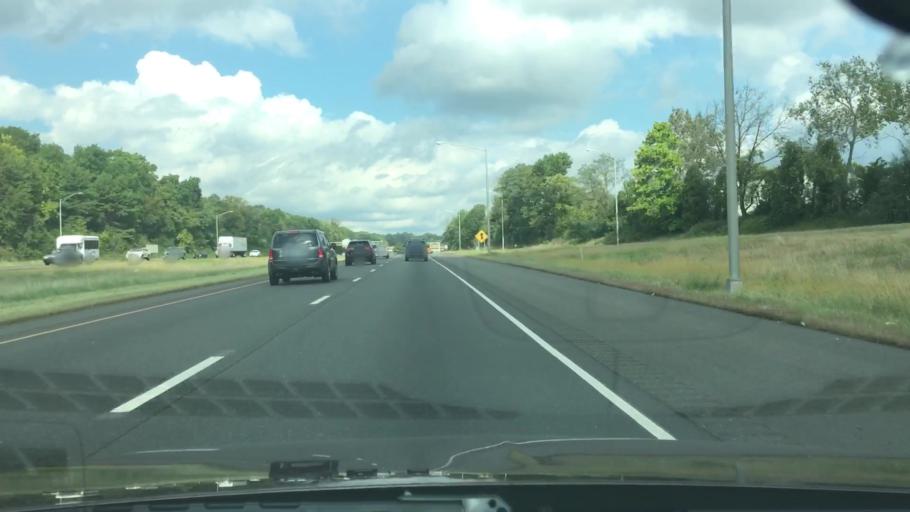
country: US
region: Connecticut
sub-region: Fairfield County
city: Trumbull
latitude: 41.2407
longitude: -73.1520
